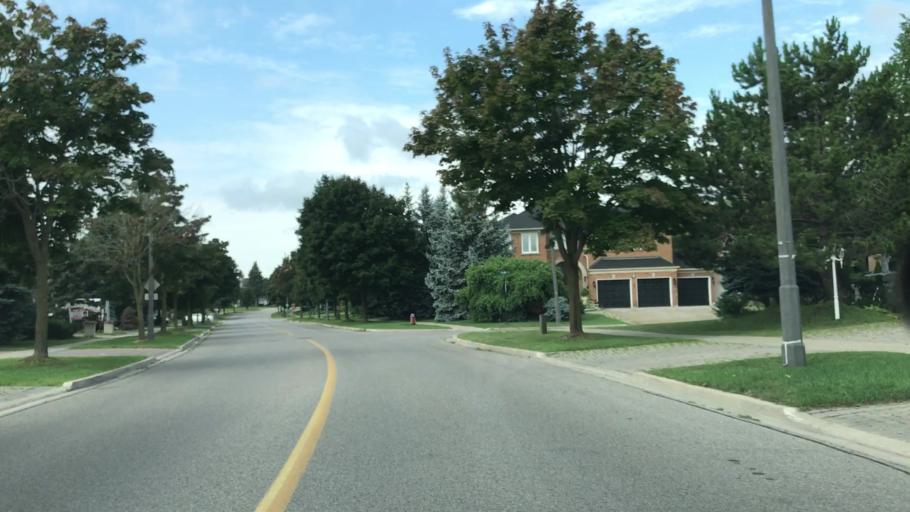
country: CA
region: Ontario
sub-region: York
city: Richmond Hill
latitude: 43.8650
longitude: -79.3976
